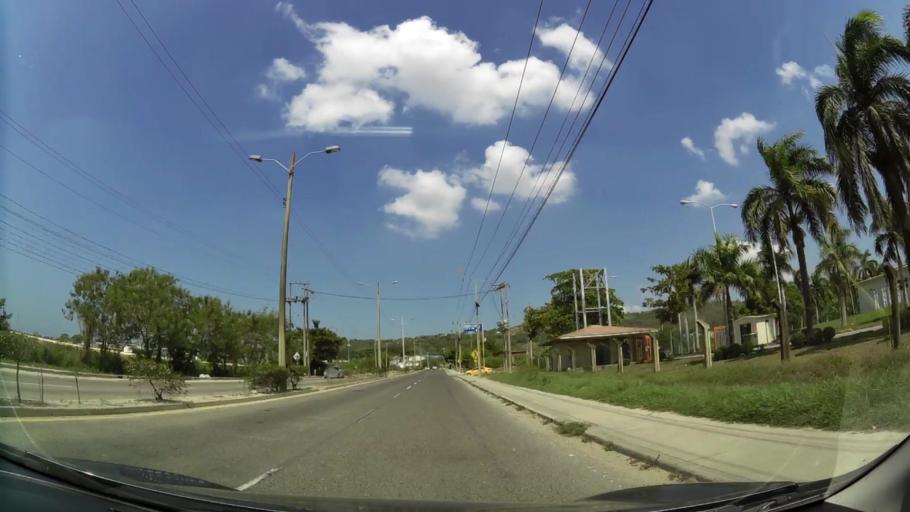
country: CO
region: Bolivar
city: Cartagena
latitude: 10.3520
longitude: -75.4959
